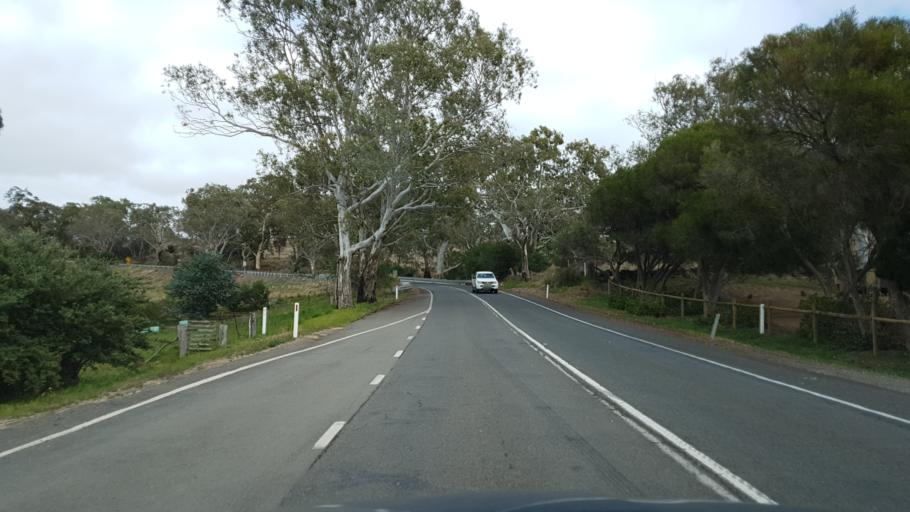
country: AU
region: South Australia
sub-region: Mount Barker
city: Nairne
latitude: -35.0405
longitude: 138.9467
